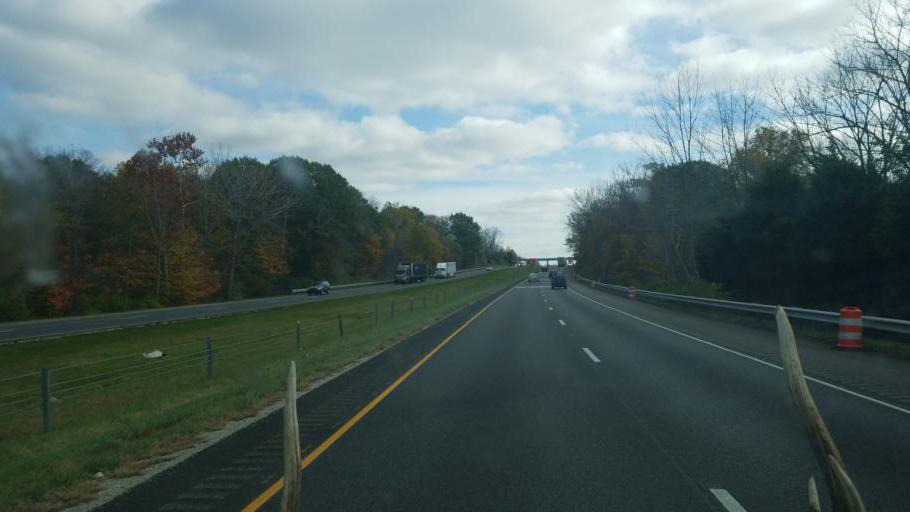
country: US
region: Ohio
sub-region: Preble County
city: New Paris
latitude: 39.8602
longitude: -84.8457
